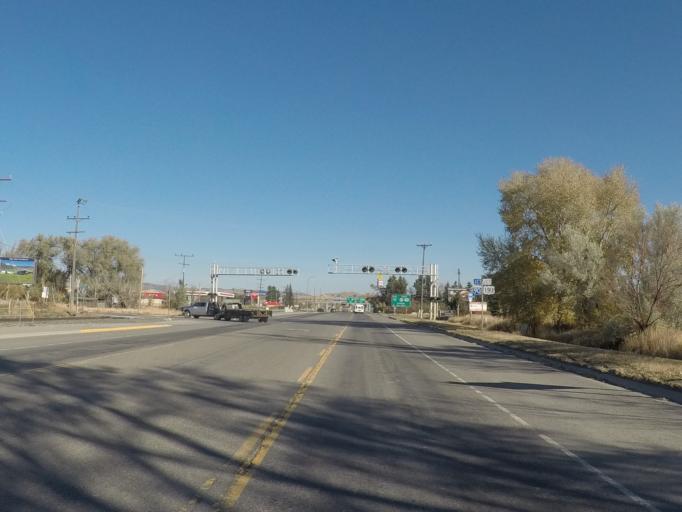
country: US
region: Montana
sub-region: Park County
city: Livingston
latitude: 45.6393
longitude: -110.5746
